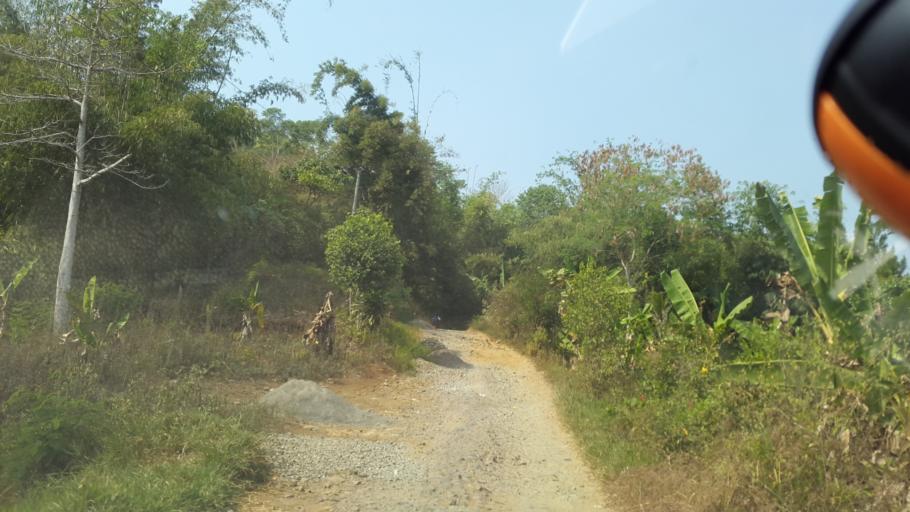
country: ID
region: West Java
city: Citampian
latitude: -7.1730
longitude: 106.7634
